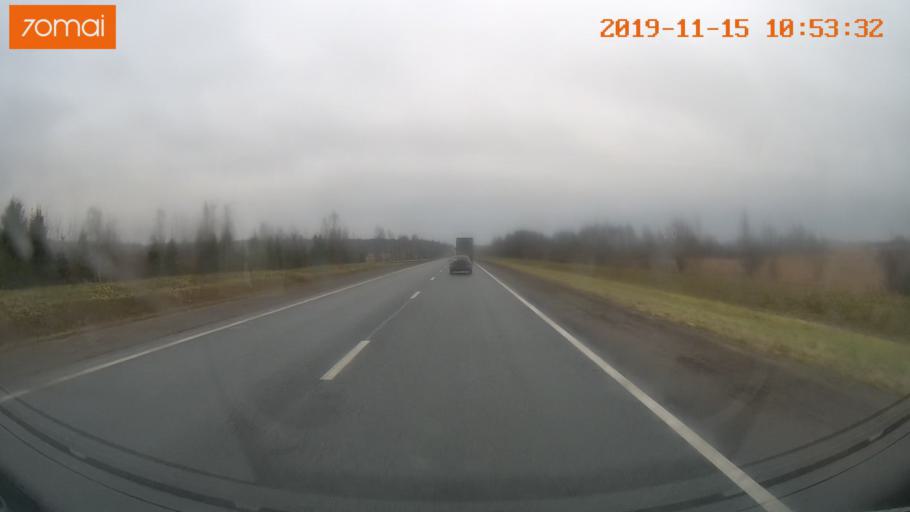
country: RU
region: Vologda
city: Chebsara
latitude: 59.1687
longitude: 38.7567
